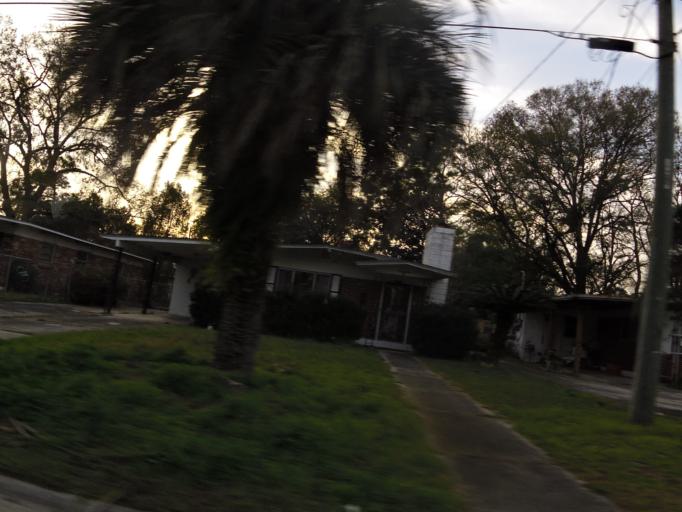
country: US
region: Florida
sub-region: Duval County
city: Jacksonville
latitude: 30.3591
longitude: -81.7051
